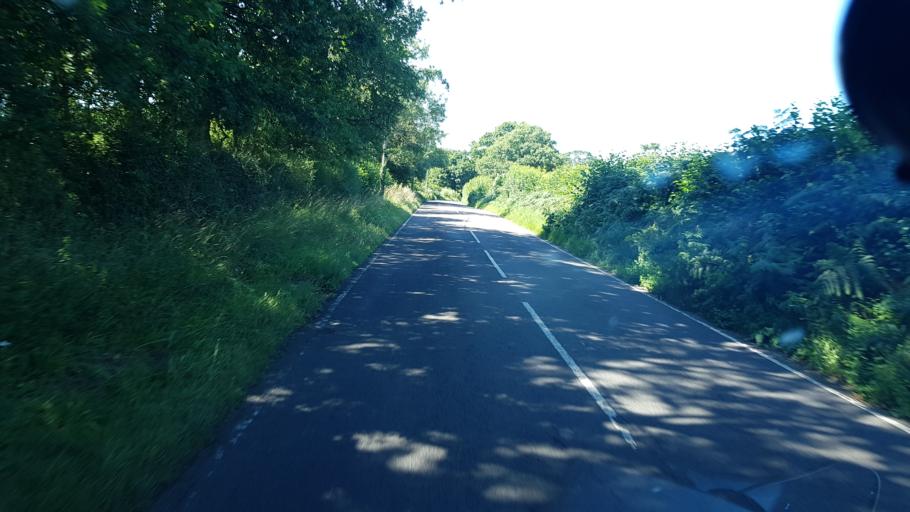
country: GB
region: England
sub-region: Kent
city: Edenbridge
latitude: 51.2179
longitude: 0.0954
